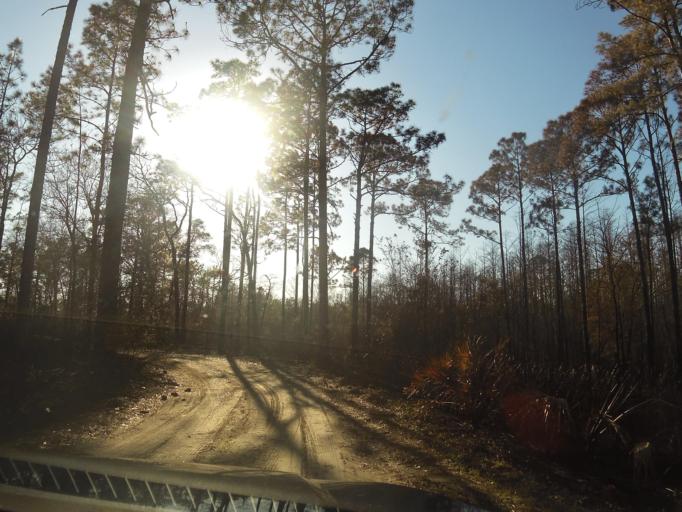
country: US
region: Florida
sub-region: Clay County
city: Middleburg
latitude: 30.1315
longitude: -81.8938
